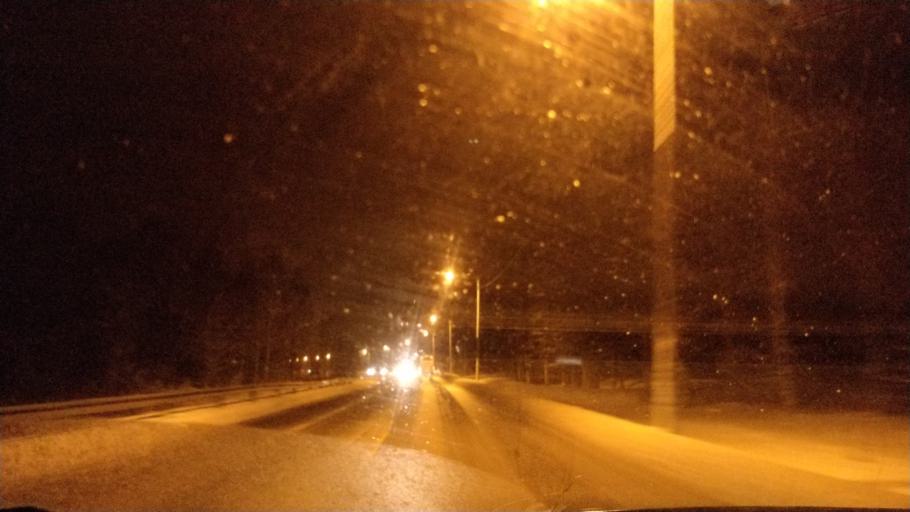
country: FI
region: Lapland
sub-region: Rovaniemi
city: Rovaniemi
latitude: 66.2873
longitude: 25.3446
